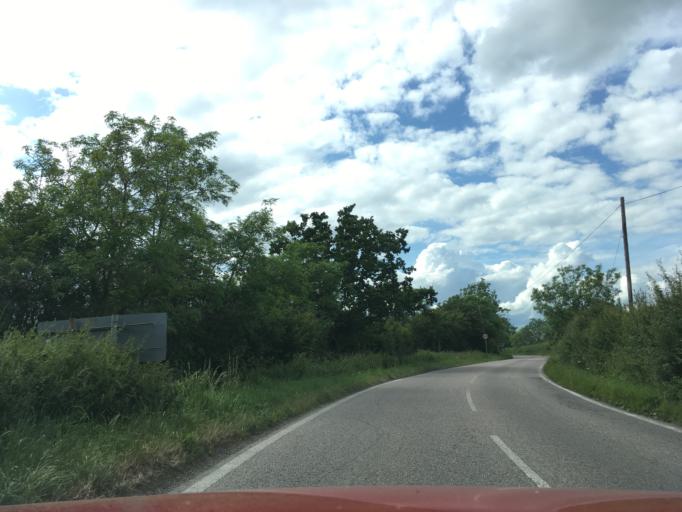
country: GB
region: England
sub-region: Wiltshire
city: Purton
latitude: 51.6044
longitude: -1.8382
